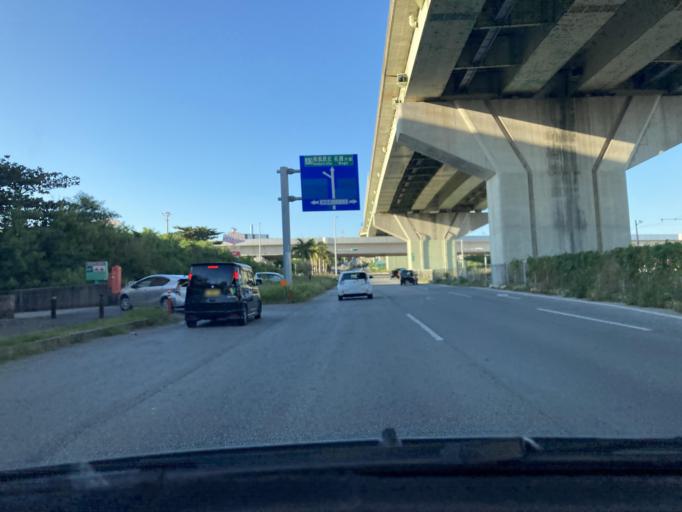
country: JP
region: Okinawa
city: Naha-shi
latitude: 26.2011
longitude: 127.7392
